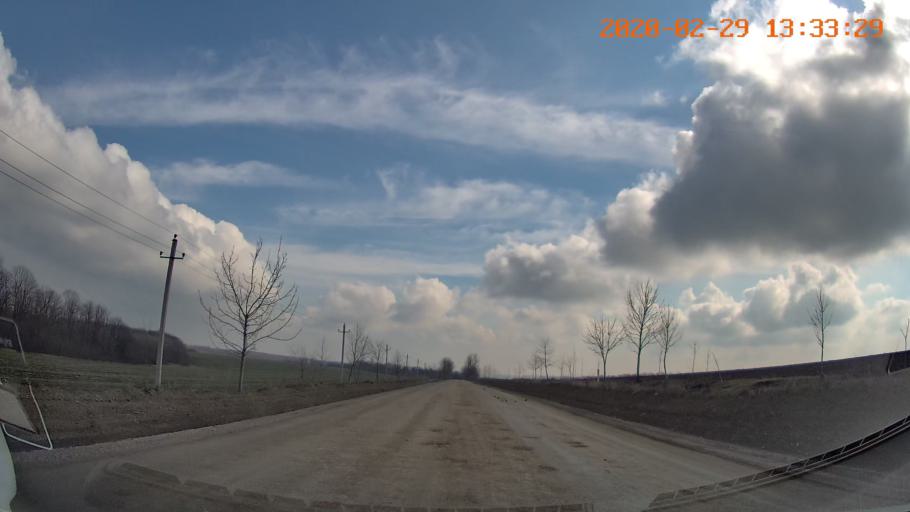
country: MD
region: Telenesti
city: Camenca
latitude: 47.8733
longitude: 28.6169
